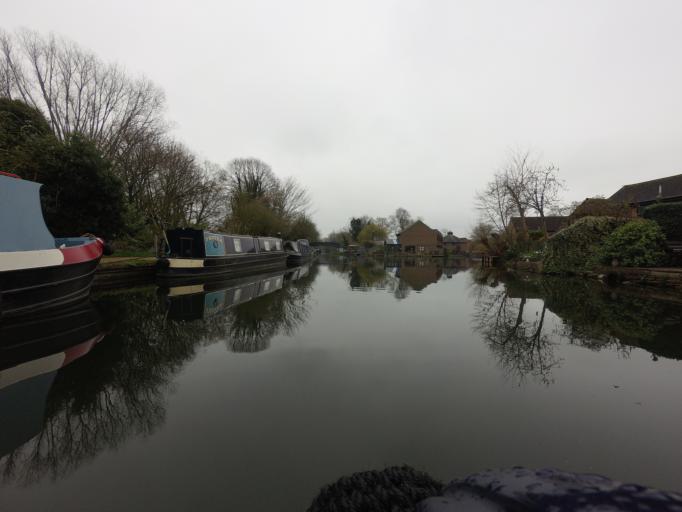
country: GB
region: England
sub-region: Hertfordshire
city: Kings Langley
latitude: 51.7162
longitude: -0.4460
